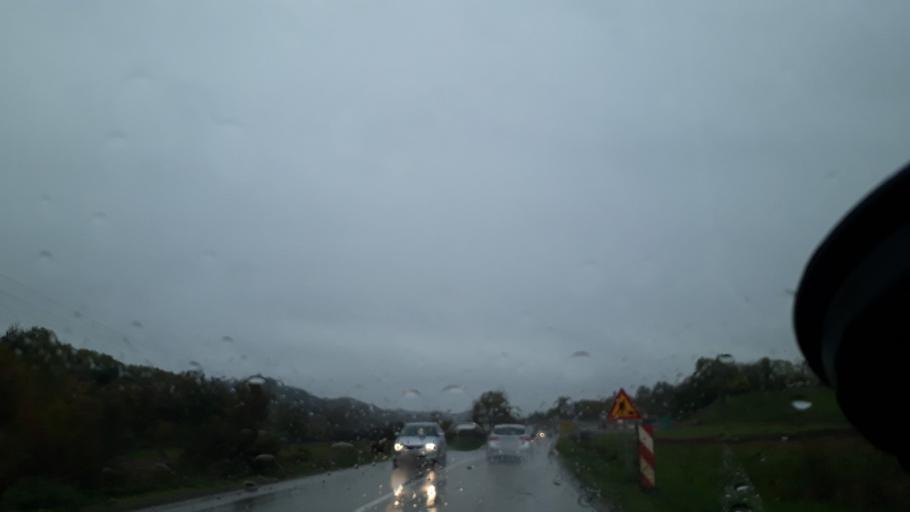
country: BA
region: Republika Srpska
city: Maglajani
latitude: 44.8682
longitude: 17.4074
